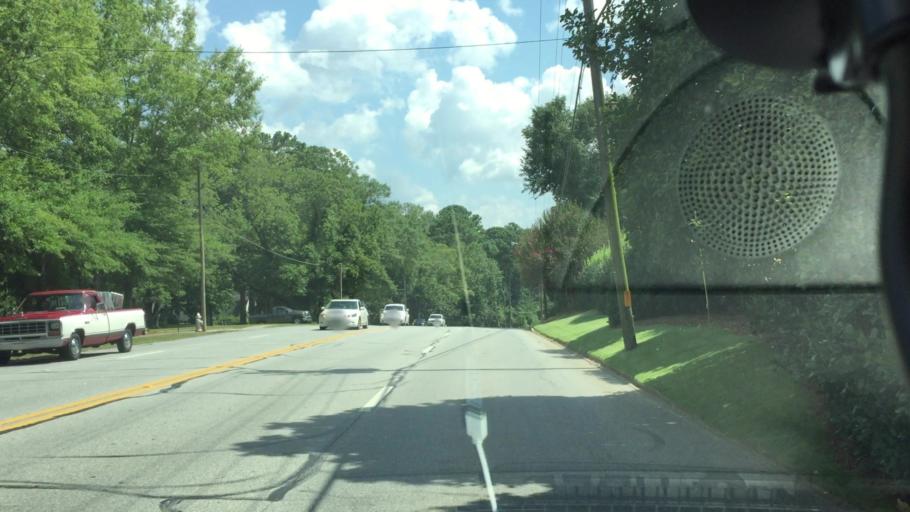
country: US
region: Alabama
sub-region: Lee County
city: Auburn
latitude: 32.5972
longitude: -85.4818
